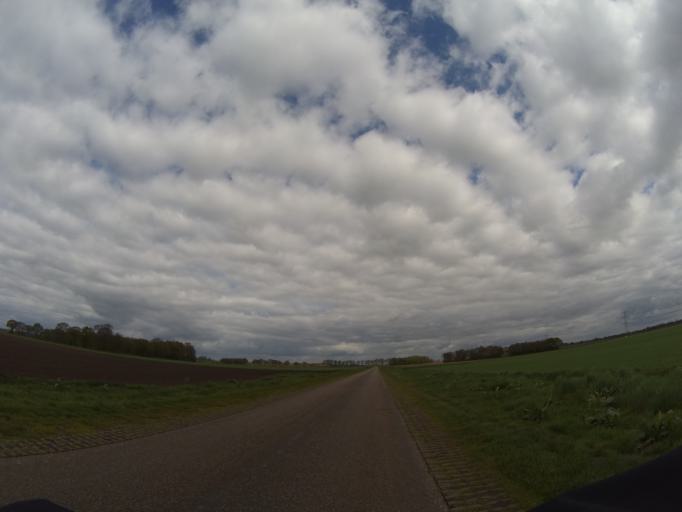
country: NL
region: Drenthe
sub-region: Gemeente Coevorden
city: Sleen
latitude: 52.7775
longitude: 6.8387
